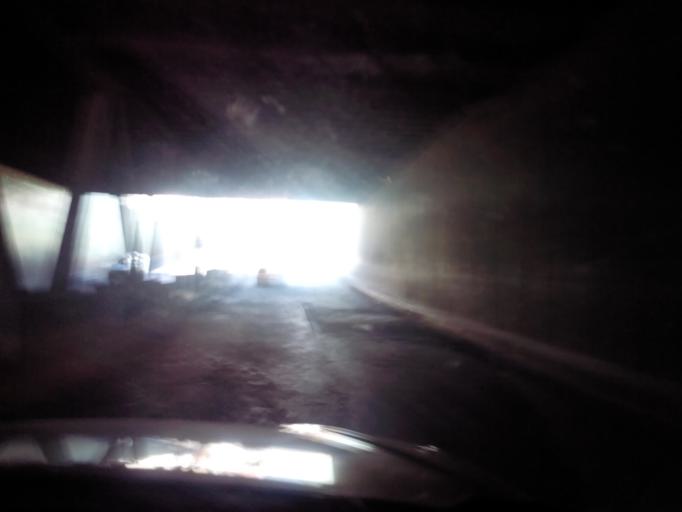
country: PE
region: Arequipa
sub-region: Provincia de Arequipa
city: Arequipa
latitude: -16.3898
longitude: -71.5476
